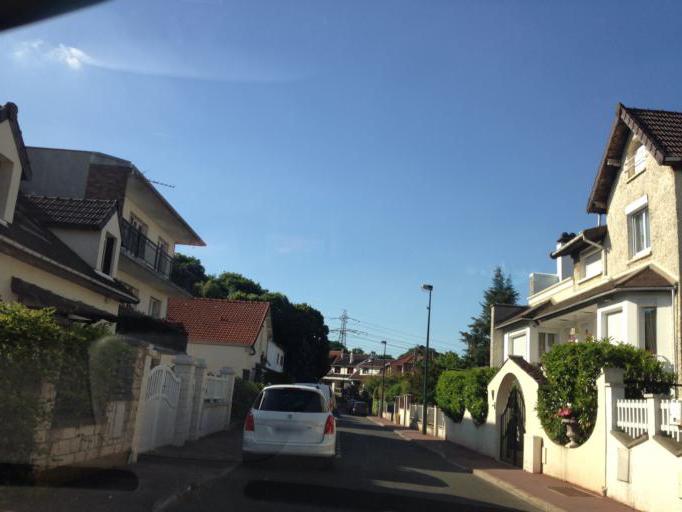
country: FR
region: Ile-de-France
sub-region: Departement des Hauts-de-Seine
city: Clamart
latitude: 48.7926
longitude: 2.2543
